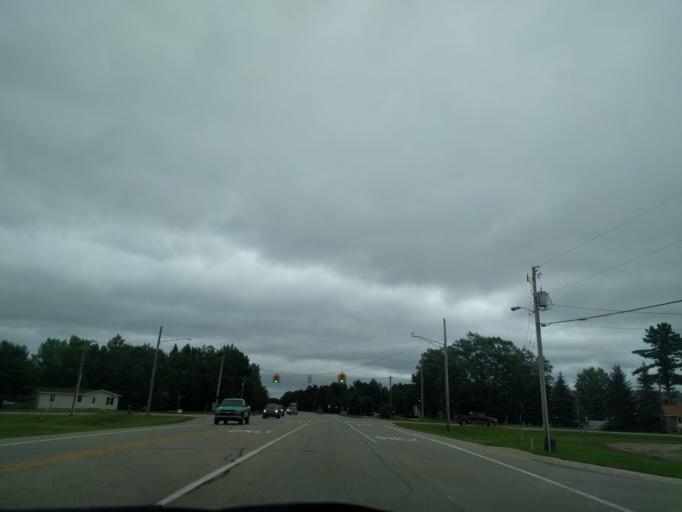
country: US
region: Michigan
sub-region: Delta County
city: Gladstone
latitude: 45.8553
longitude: -87.0491
